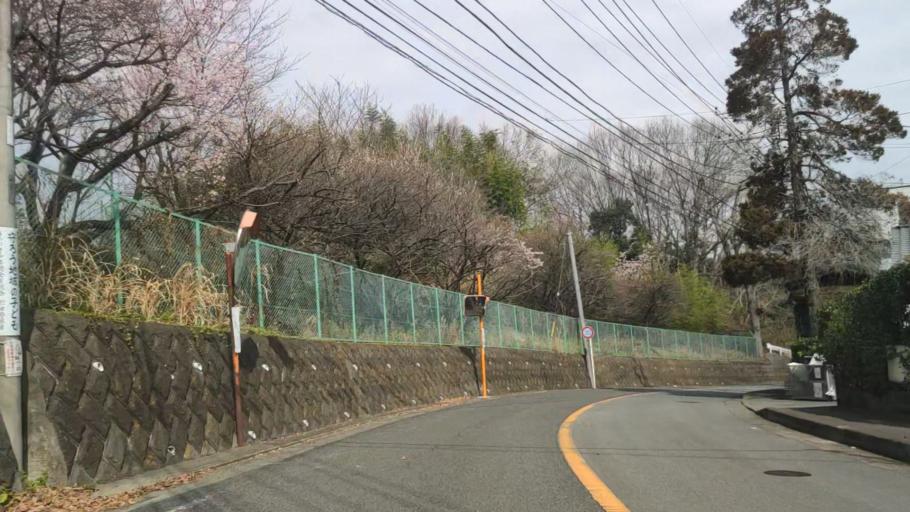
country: JP
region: Kanagawa
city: Hadano
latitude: 35.3370
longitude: 139.2270
